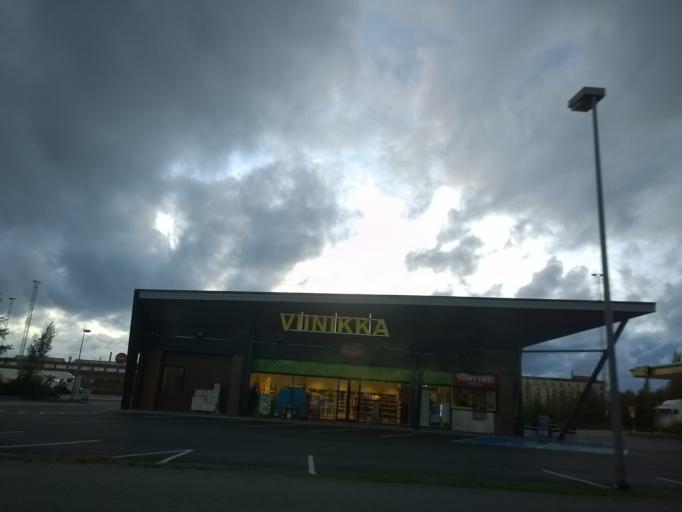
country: FI
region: Pirkanmaa
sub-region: Tampere
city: Tampere
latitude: 61.4853
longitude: 23.7774
